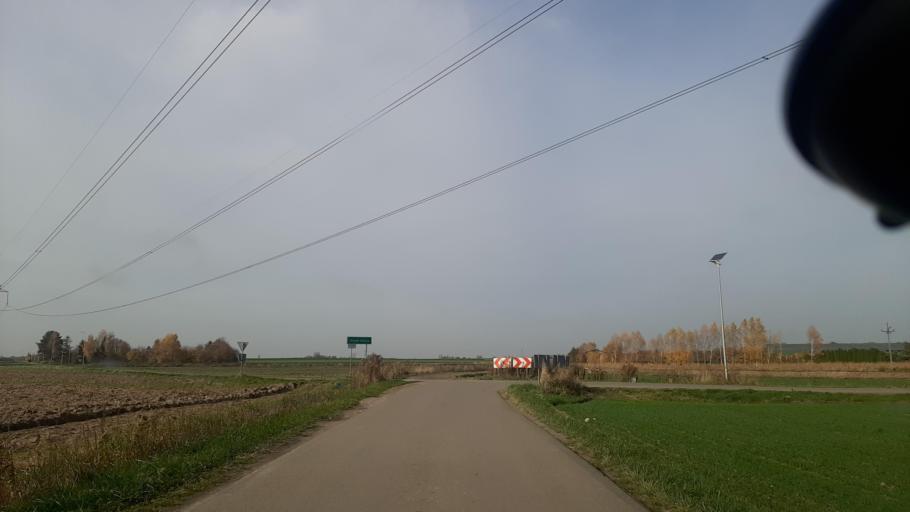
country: PL
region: Lublin Voivodeship
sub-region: Powiat lubelski
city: Lublin
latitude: 51.3326
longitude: 22.5415
